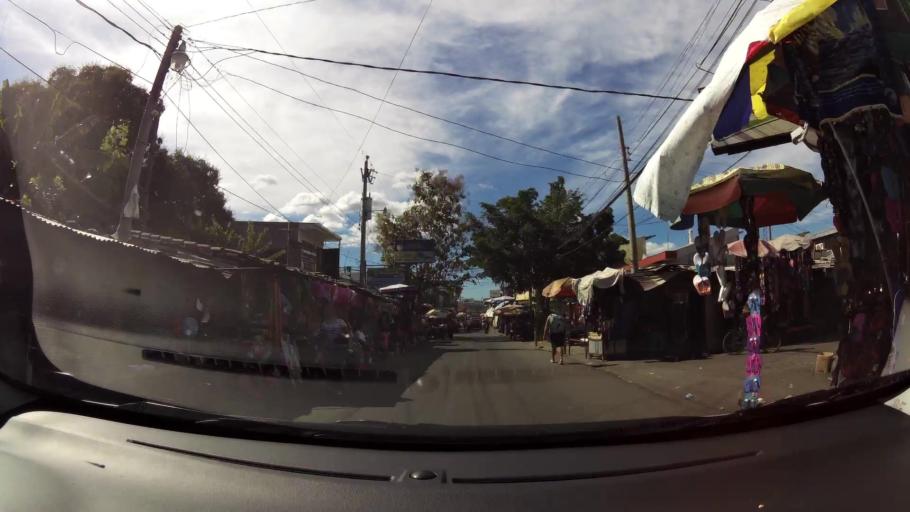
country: SV
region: San Salvador
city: Aguilares
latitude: 13.9572
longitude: -89.1853
